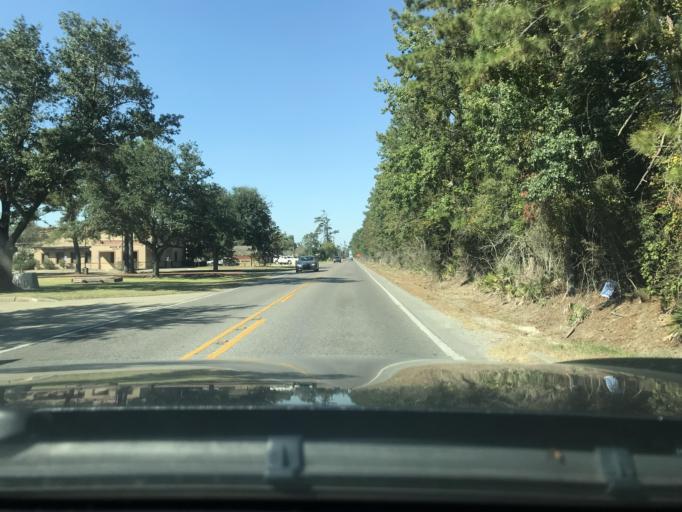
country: US
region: Louisiana
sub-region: Calcasieu Parish
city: Moss Bluff
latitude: 30.3026
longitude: -93.2001
